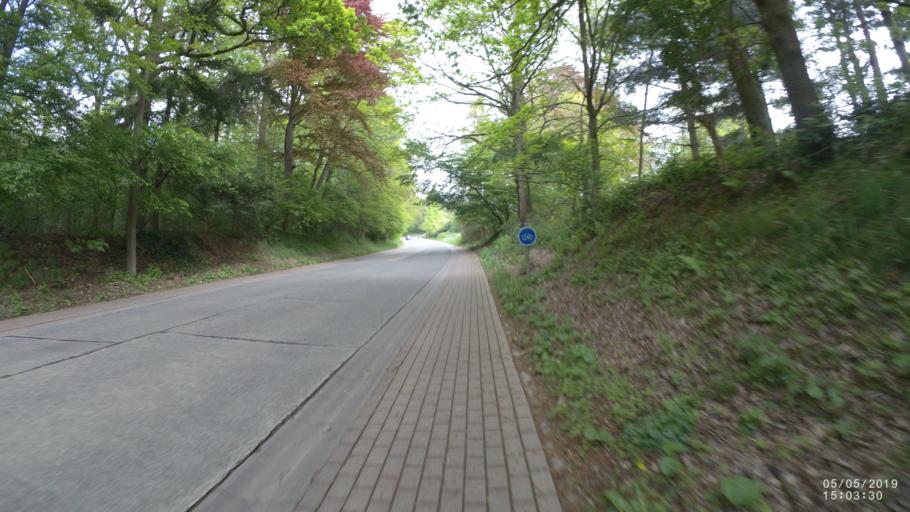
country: BE
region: Flanders
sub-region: Provincie Vlaams-Brabant
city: Lubbeek
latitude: 50.8807
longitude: 4.8654
